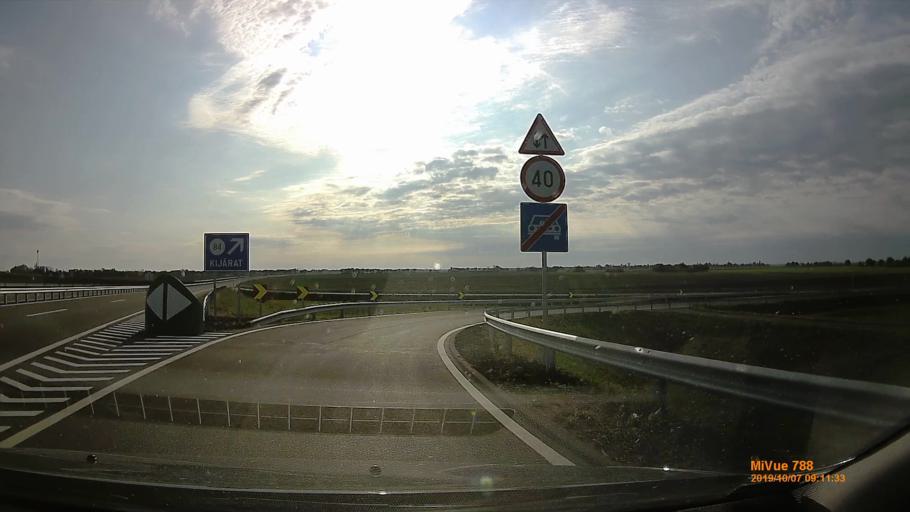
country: HU
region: Bekes
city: Nagyszenas
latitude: 46.8117
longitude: 20.6768
